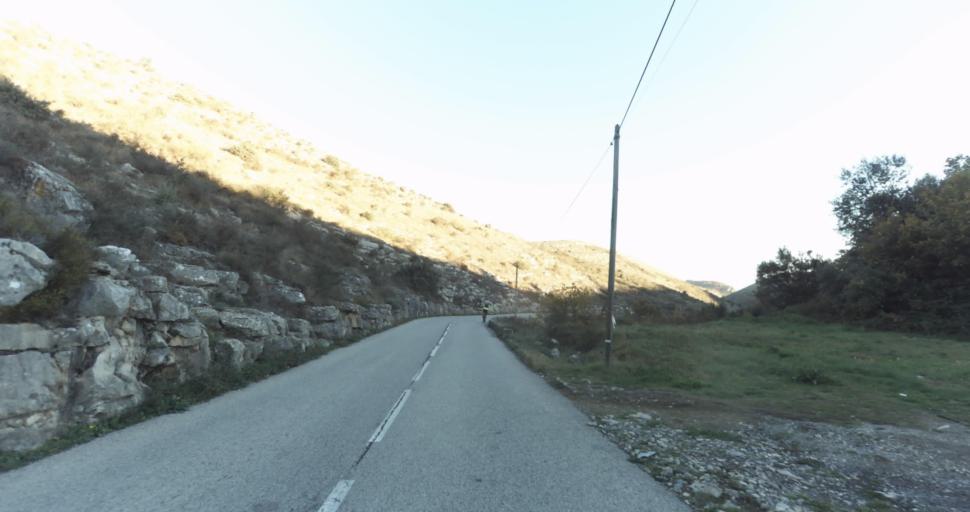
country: FR
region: Provence-Alpes-Cote d'Azur
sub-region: Departement des Alpes-Maritimes
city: Vence
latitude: 43.7544
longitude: 7.0934
